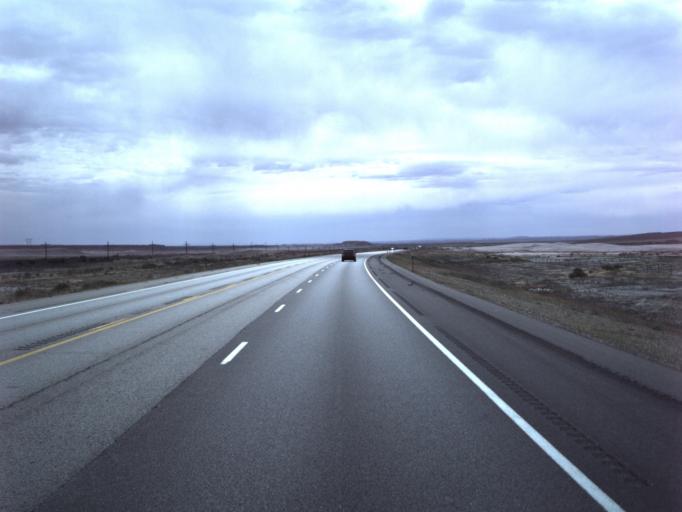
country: US
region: Utah
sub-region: Carbon County
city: East Carbon City
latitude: 39.1195
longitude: -110.3299
